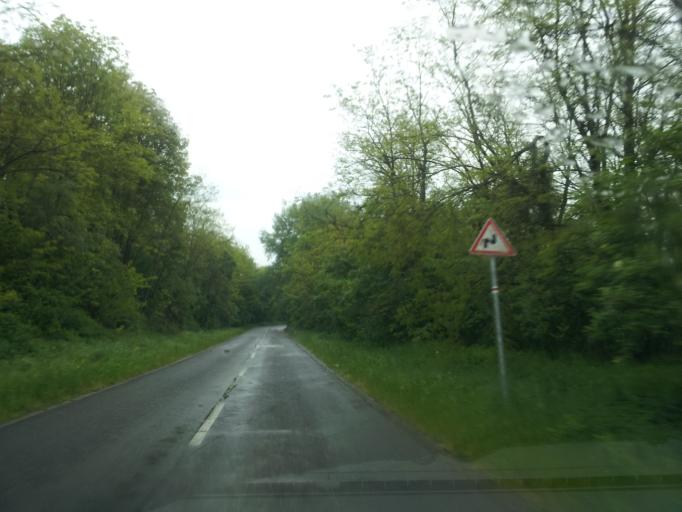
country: HU
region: Tolna
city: Bonyhad
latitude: 46.2621
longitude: 18.6093
